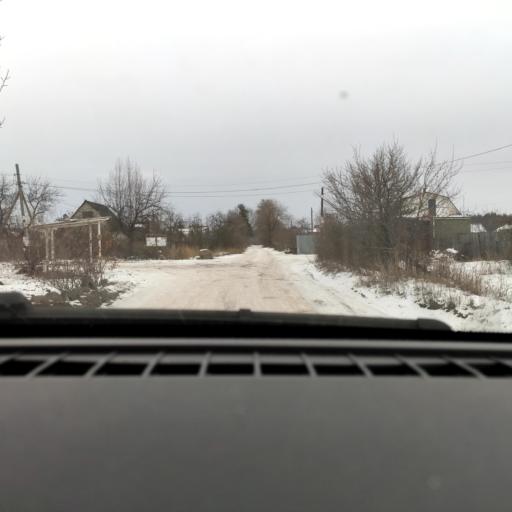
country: RU
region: Voronezj
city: Maslovka
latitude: 51.6022
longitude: 39.2844
